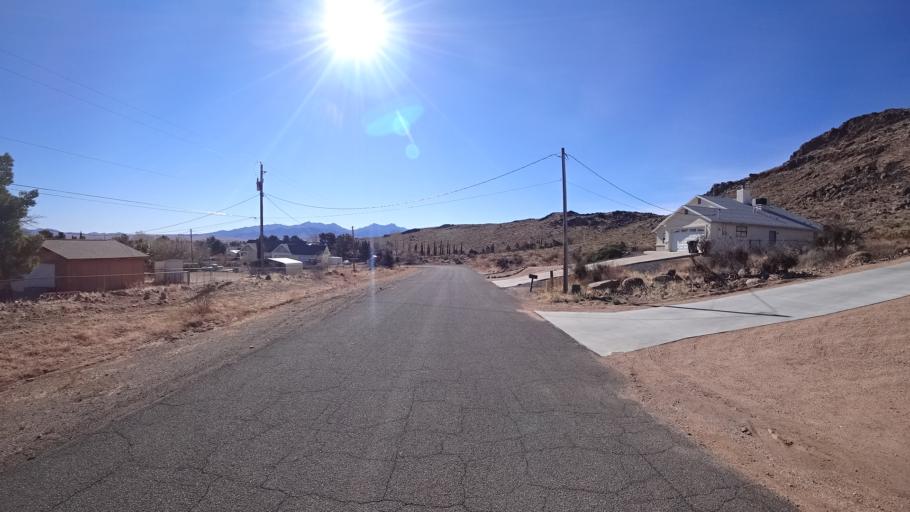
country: US
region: Arizona
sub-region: Mohave County
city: New Kingman-Butler
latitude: 35.2618
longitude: -114.0471
